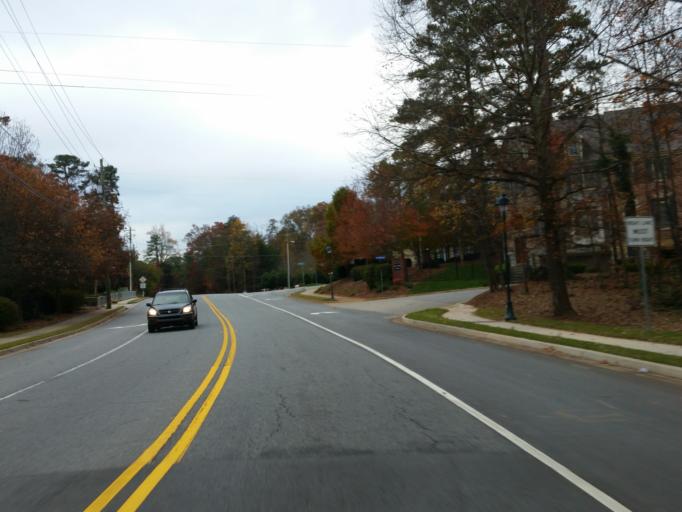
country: US
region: Georgia
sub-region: Fulton County
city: Sandy Springs
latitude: 33.9068
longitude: -84.3671
